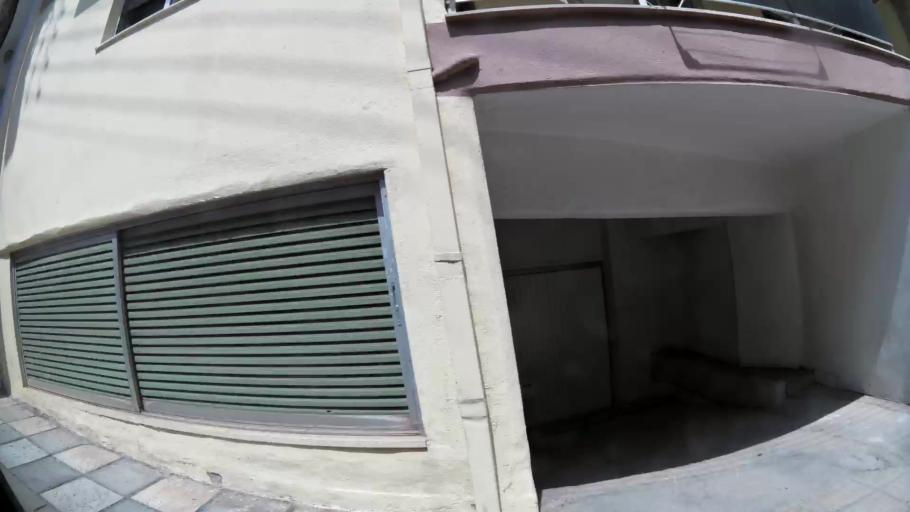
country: GR
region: West Macedonia
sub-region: Nomos Kozanis
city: Kozani
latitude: 40.3050
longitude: 21.7889
